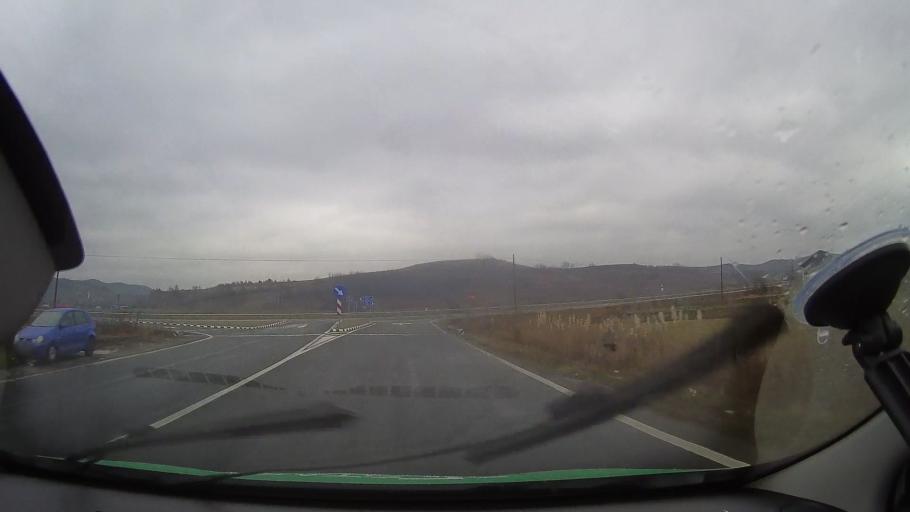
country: RO
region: Hunedoara
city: Vata de Jos
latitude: 46.1916
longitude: 22.6079
